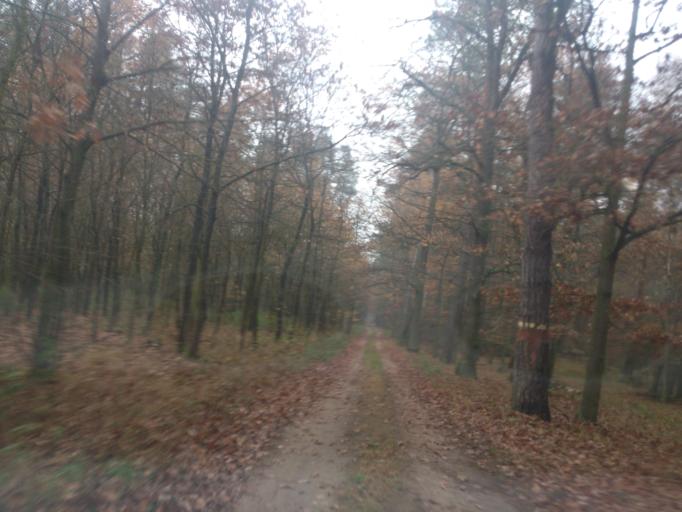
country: PL
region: Kujawsko-Pomorskie
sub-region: Powiat golubsko-dobrzynski
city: Radomin
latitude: 53.1390
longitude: 19.1342
